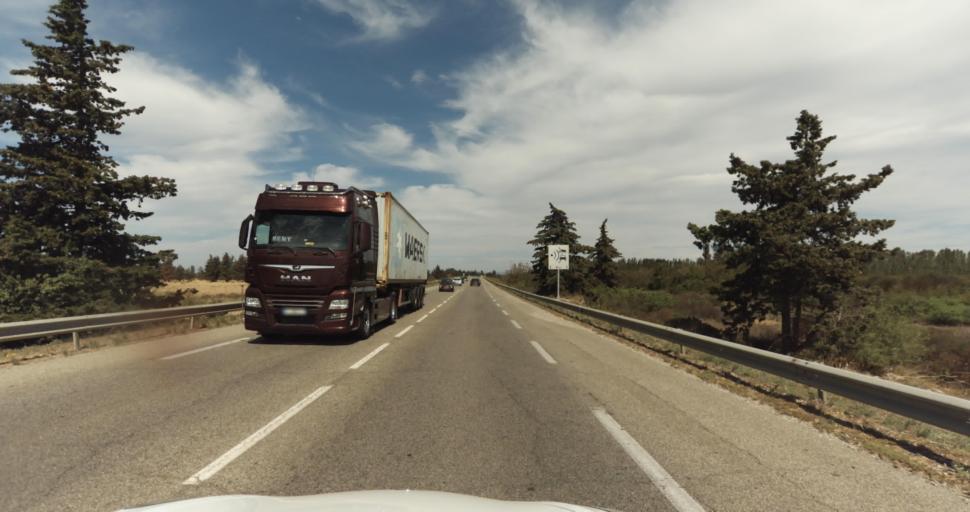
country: FR
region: Provence-Alpes-Cote d'Azur
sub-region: Departement des Bouches-du-Rhone
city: Istres
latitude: 43.5384
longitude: 4.9573
